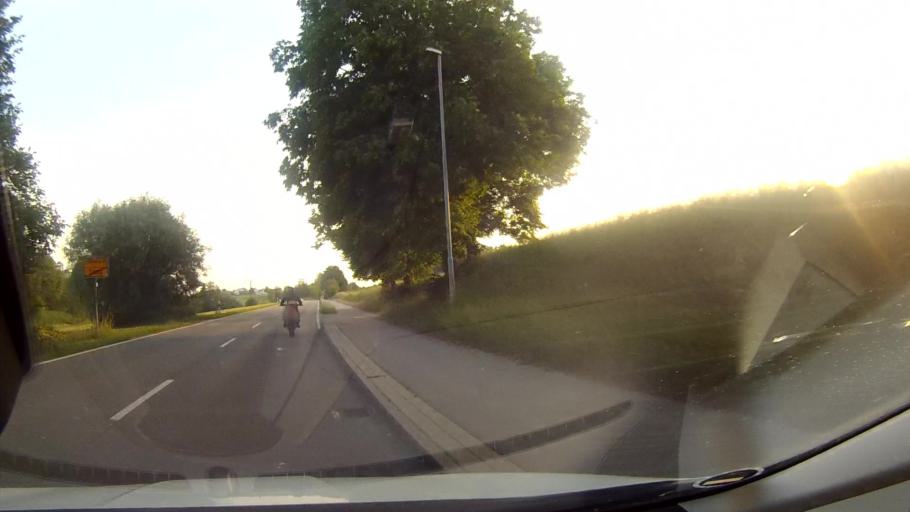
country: DE
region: Baden-Wuerttemberg
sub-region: Tuebingen Region
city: Staig
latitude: 48.2976
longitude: 9.9857
